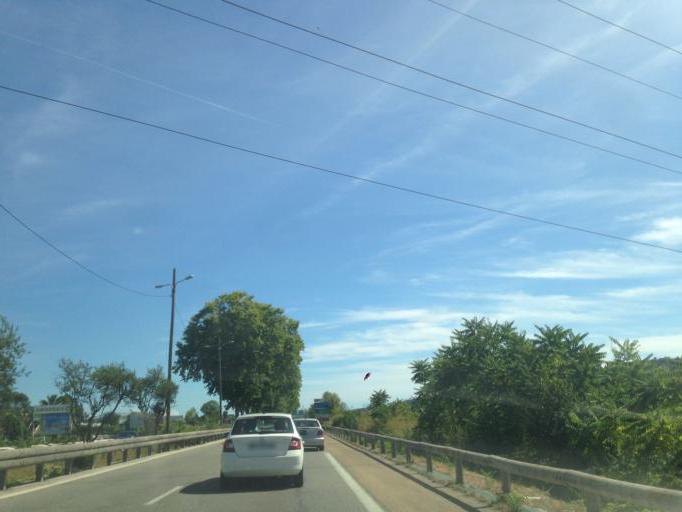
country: FR
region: Provence-Alpes-Cote d'Azur
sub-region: Departement des Alpes-Maritimes
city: La Gaude
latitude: 43.7173
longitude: 7.1866
